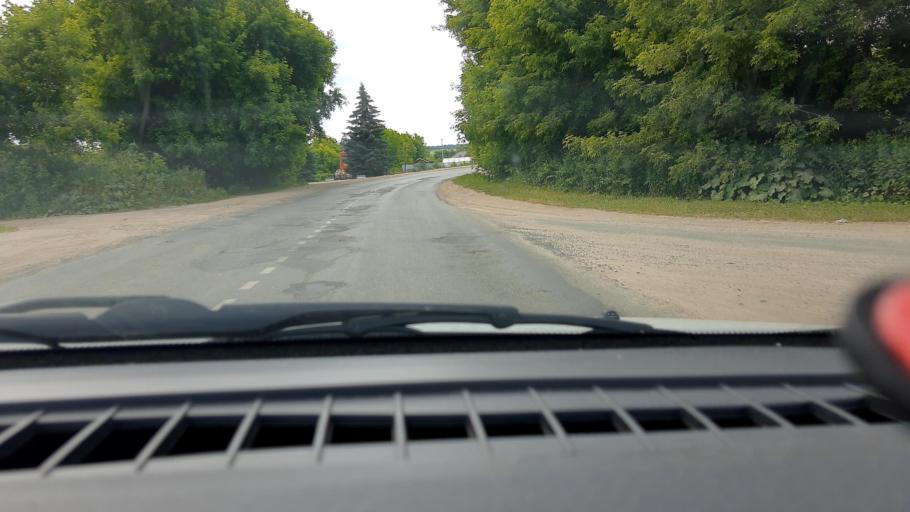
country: RU
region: Nizjnij Novgorod
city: Kstovo
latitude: 56.1312
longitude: 44.0848
